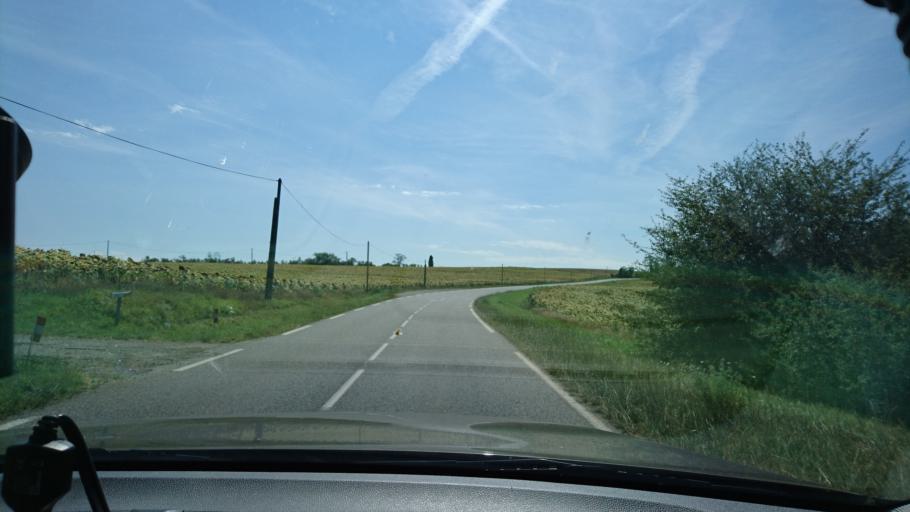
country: FR
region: Midi-Pyrenees
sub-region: Departement de la Haute-Garonne
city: Saint-Sulpice-sur-Leze
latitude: 43.3337
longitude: 1.3099
